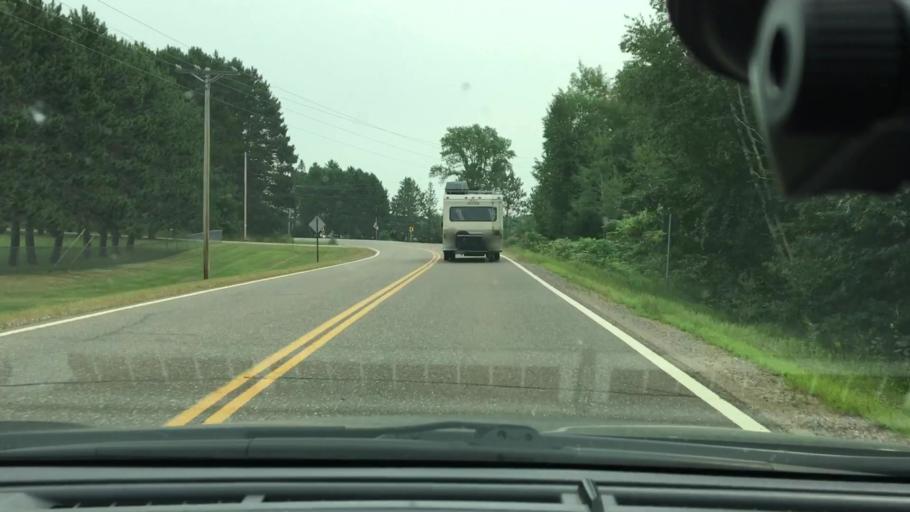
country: US
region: Minnesota
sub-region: Aitkin County
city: Aitkin
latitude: 46.4010
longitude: -93.7712
